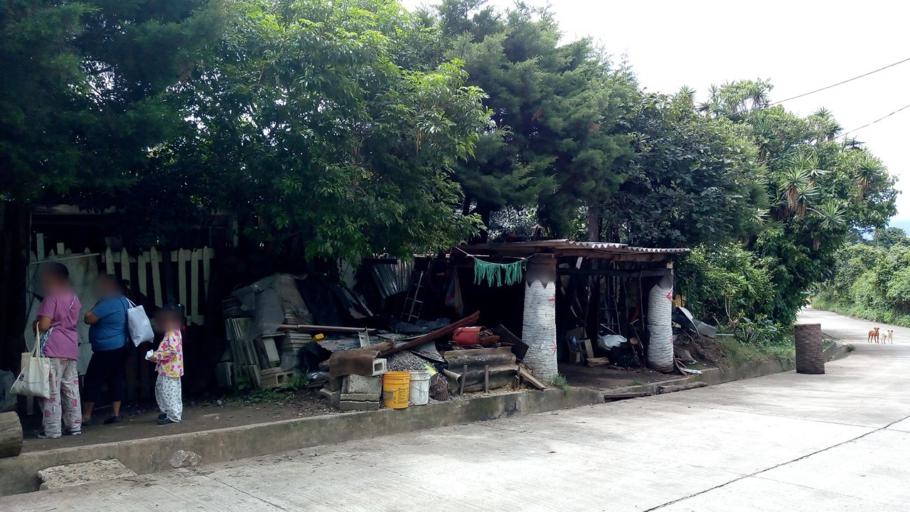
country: GT
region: Guatemala
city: Villa Canales
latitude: 14.5117
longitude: -90.5179
